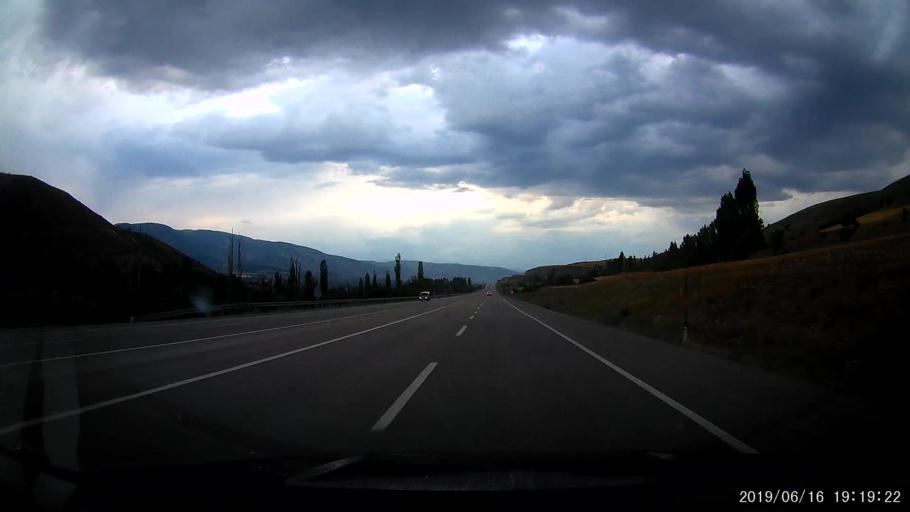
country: TR
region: Sivas
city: Akincilar
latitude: 40.0944
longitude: 38.4316
